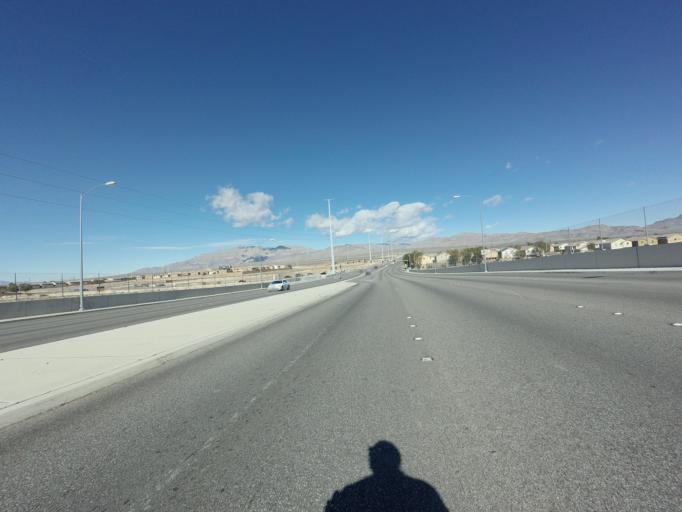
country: US
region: Nevada
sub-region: Clark County
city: Nellis Air Force Base
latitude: 36.2677
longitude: -115.0797
